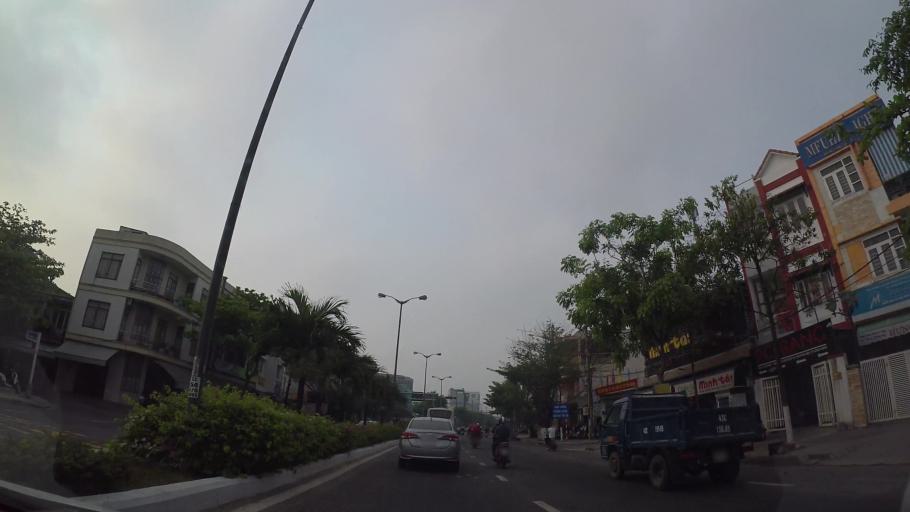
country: VN
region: Da Nang
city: Cam Le
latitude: 16.0321
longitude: 108.2242
